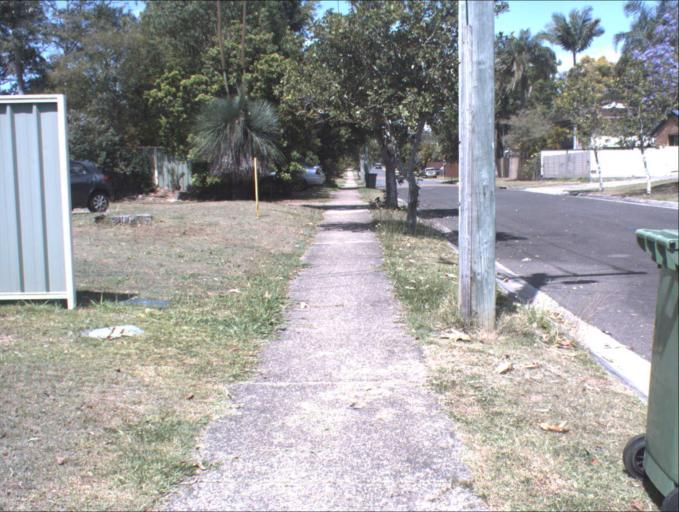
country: AU
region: Queensland
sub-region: Logan
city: Slacks Creek
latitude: -27.6410
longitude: 153.1467
